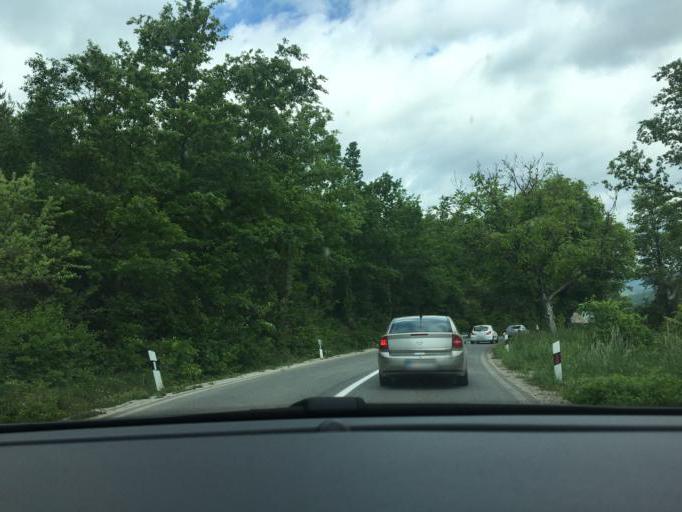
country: MK
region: Resen
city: Jankovec
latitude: 41.1195
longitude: 21.0097
